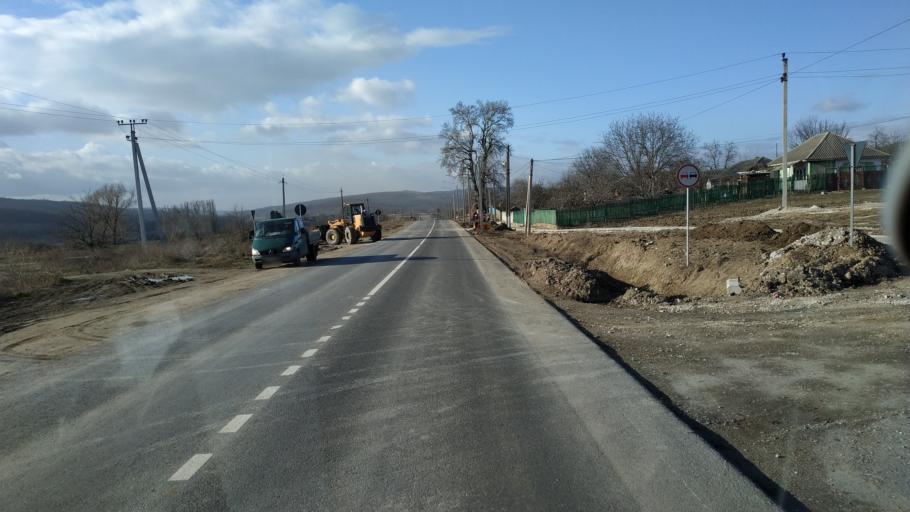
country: MD
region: Calarasi
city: Calarasi
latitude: 47.3156
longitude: 28.1162
